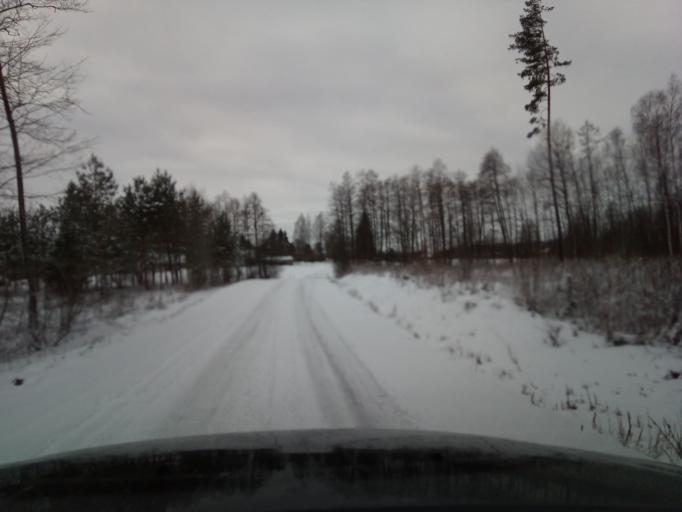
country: LT
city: Zarasai
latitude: 55.6754
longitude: 25.9838
